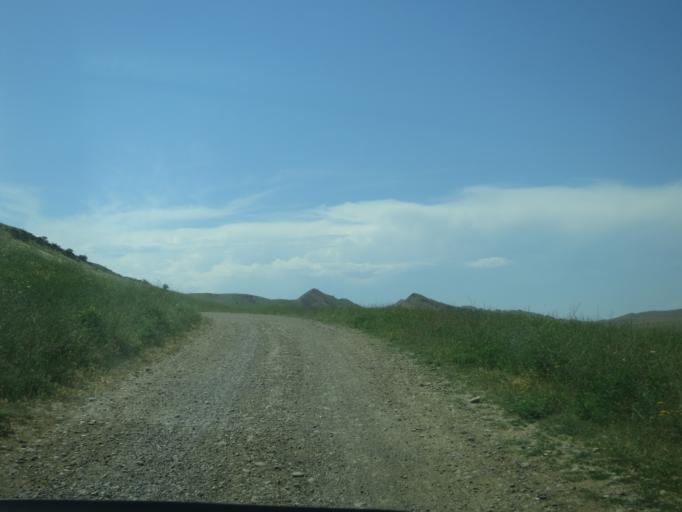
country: AZ
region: Agstafa
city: Saloglu
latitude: 41.4570
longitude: 45.3631
